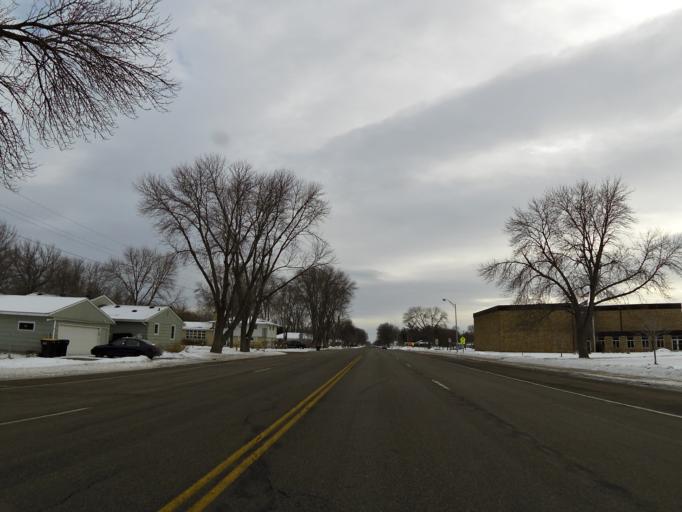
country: US
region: Minnesota
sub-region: Scott County
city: Shakopee
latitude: 44.7883
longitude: -93.5240
